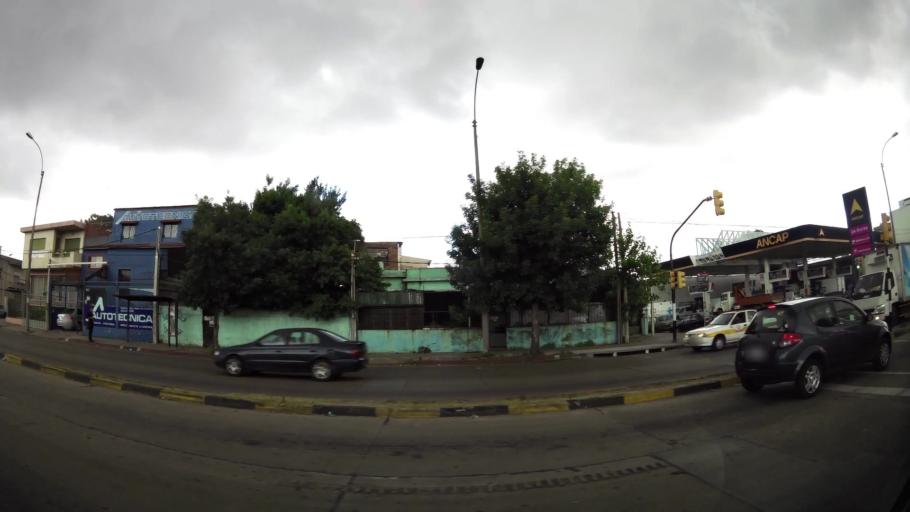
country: UY
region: Montevideo
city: Montevideo
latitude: -34.8654
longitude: -56.1660
